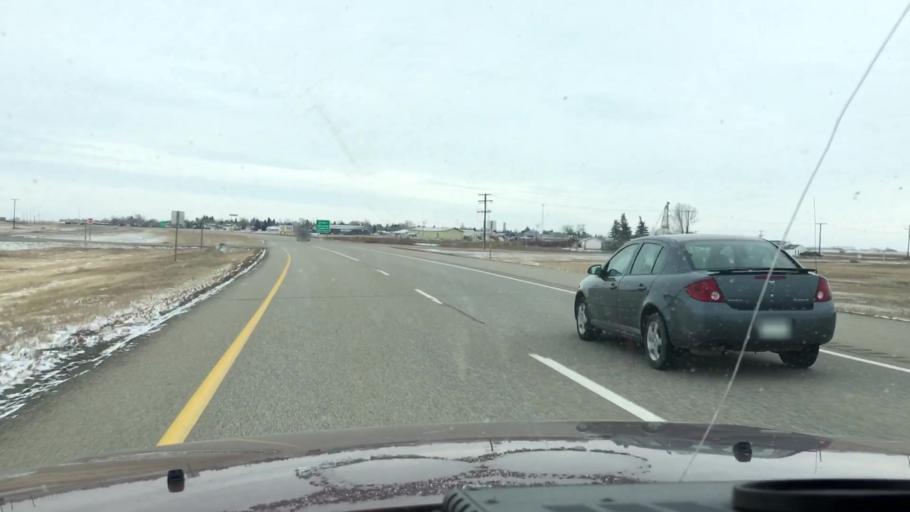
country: CA
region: Saskatchewan
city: Watrous
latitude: 51.2737
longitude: -106.0053
